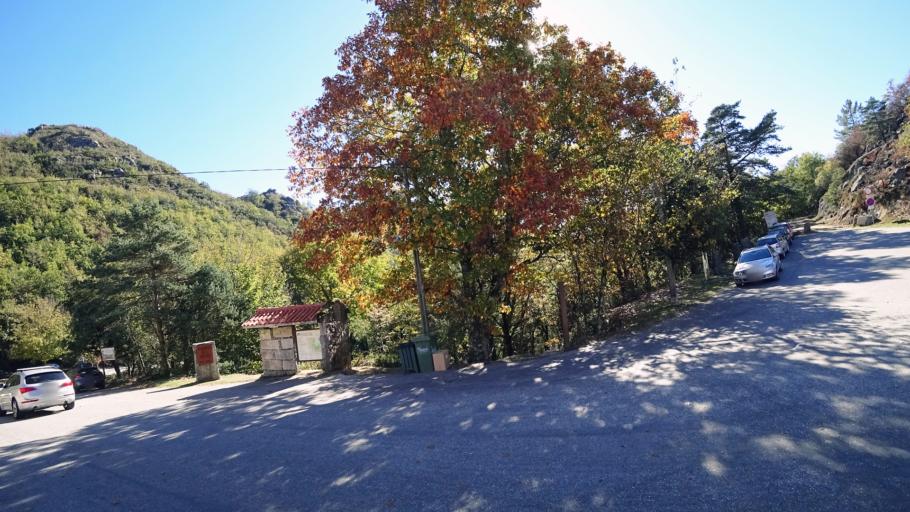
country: ES
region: Galicia
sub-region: Provincia de Ourense
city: Lobios
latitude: 41.8084
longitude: -8.1314
